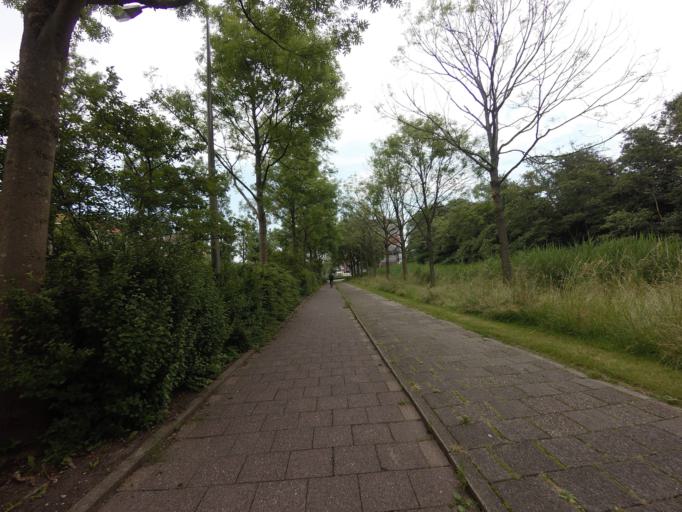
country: NL
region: North Holland
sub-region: Gemeente Purmerend
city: Purmerend
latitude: 52.5032
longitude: 4.9631
